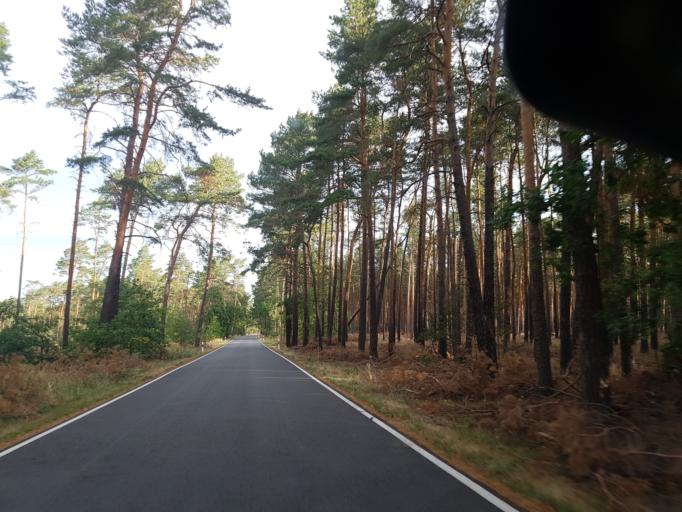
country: DE
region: Saxony-Anhalt
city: Holzdorf
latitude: 51.7927
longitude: 13.1037
